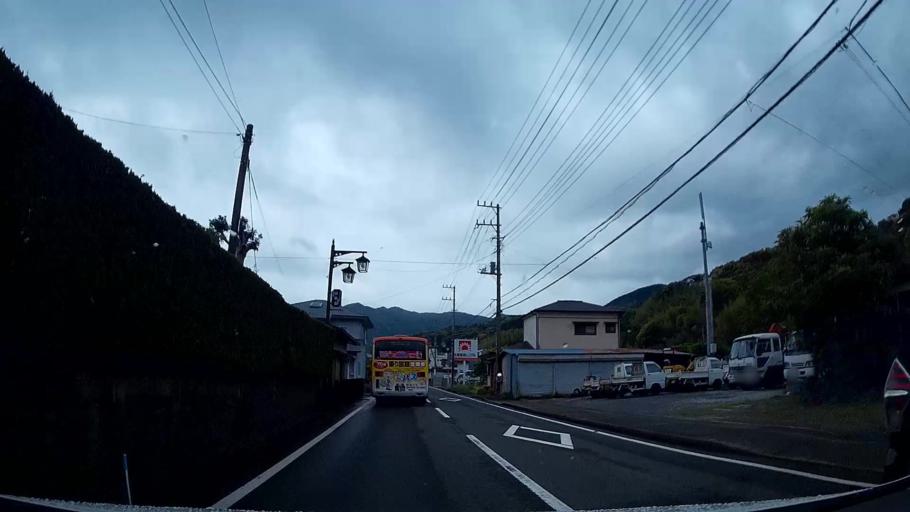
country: JP
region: Shizuoka
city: Shimoda
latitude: 34.7599
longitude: 138.9822
